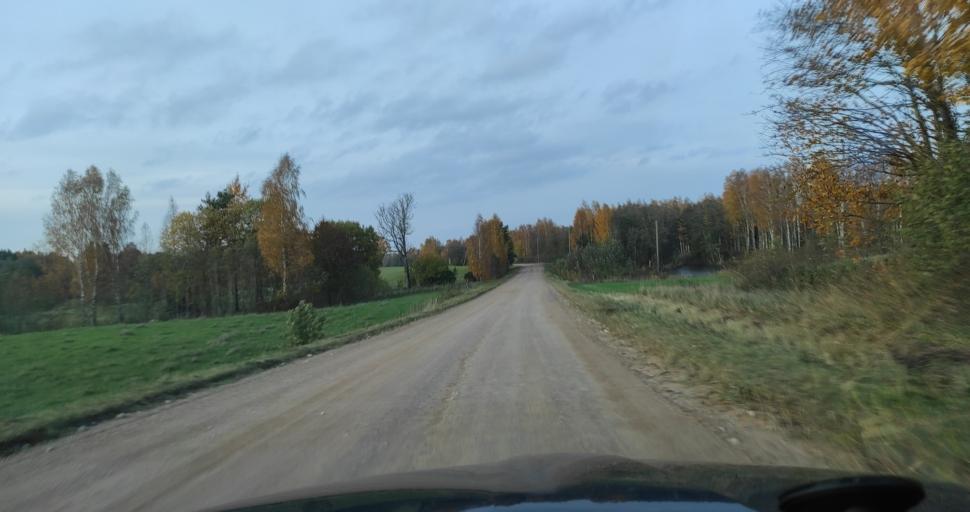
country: LV
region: Aizpute
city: Aizpute
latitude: 56.6600
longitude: 21.7961
